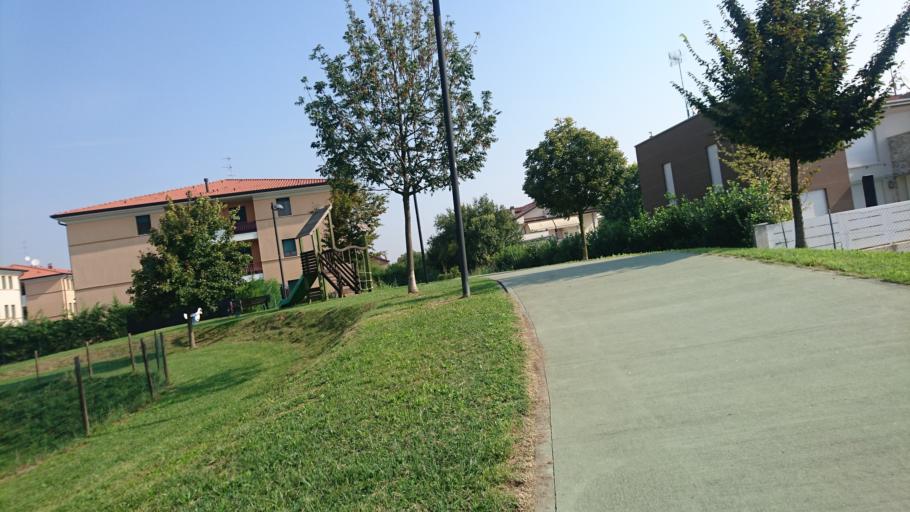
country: IT
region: Veneto
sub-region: Provincia di Padova
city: Masera di Padova
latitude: 45.3428
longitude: 11.8637
